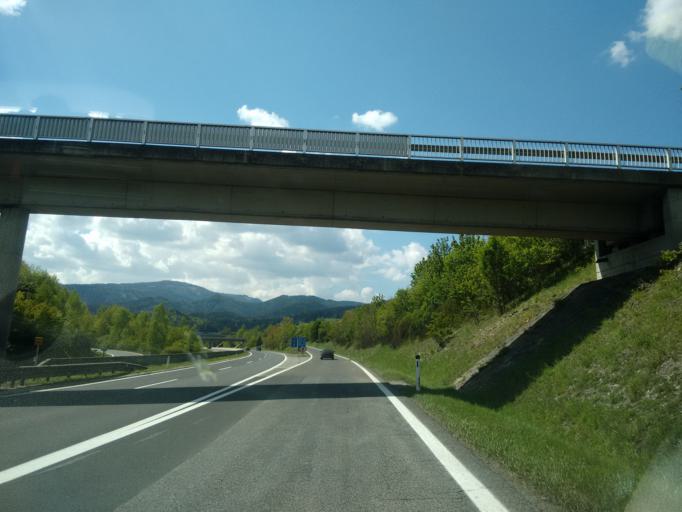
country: AT
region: Styria
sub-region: Politischer Bezirk Leoben
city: Sankt Michael in Obersteiermark
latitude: 47.3363
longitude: 15.0167
